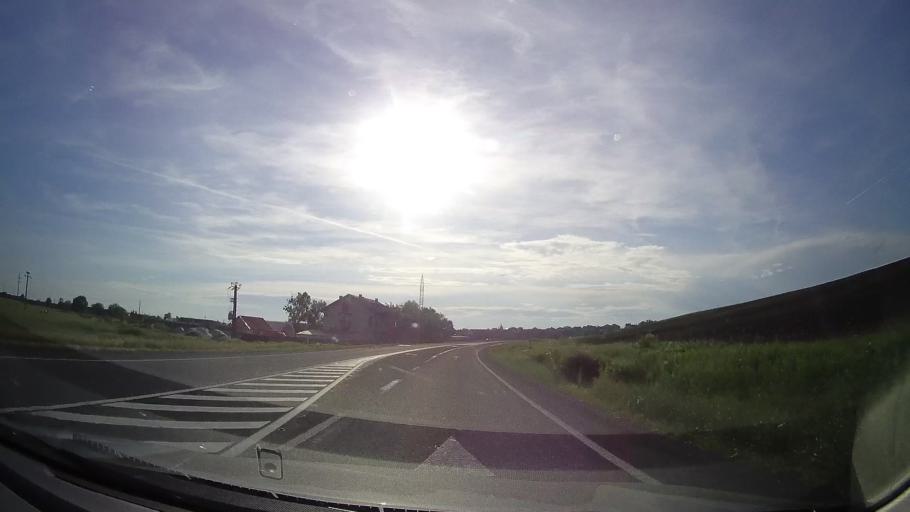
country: RO
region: Timis
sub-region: Oras Recas
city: Recas
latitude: 45.7965
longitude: 21.5228
